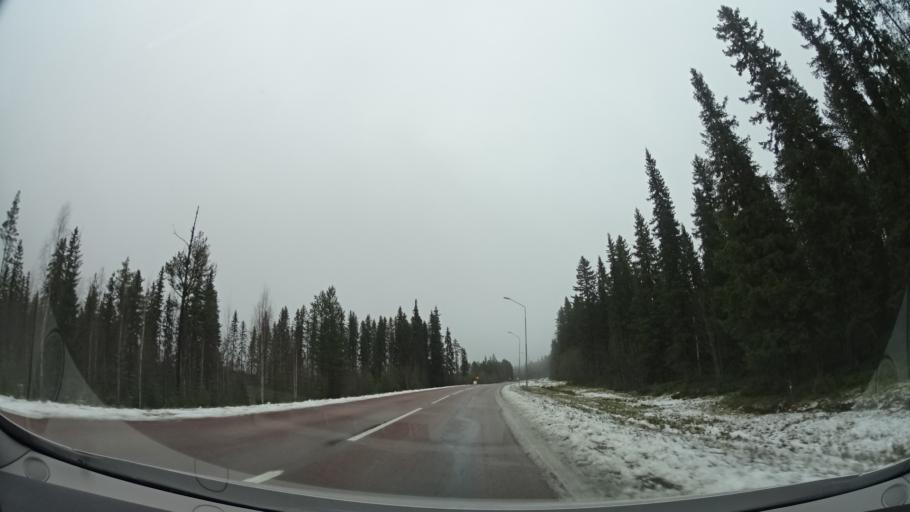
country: SE
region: Vaesterbotten
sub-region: Dorotea Kommun
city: Dorotea
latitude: 64.1240
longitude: 16.2129
